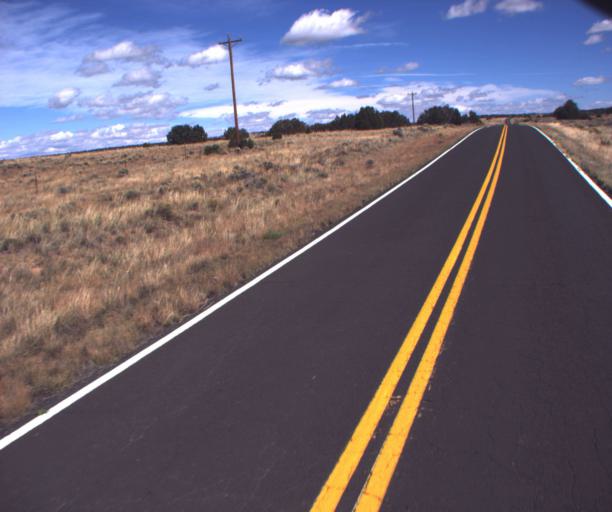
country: US
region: New Mexico
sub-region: McKinley County
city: Zuni Pueblo
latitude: 34.9753
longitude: -109.1346
